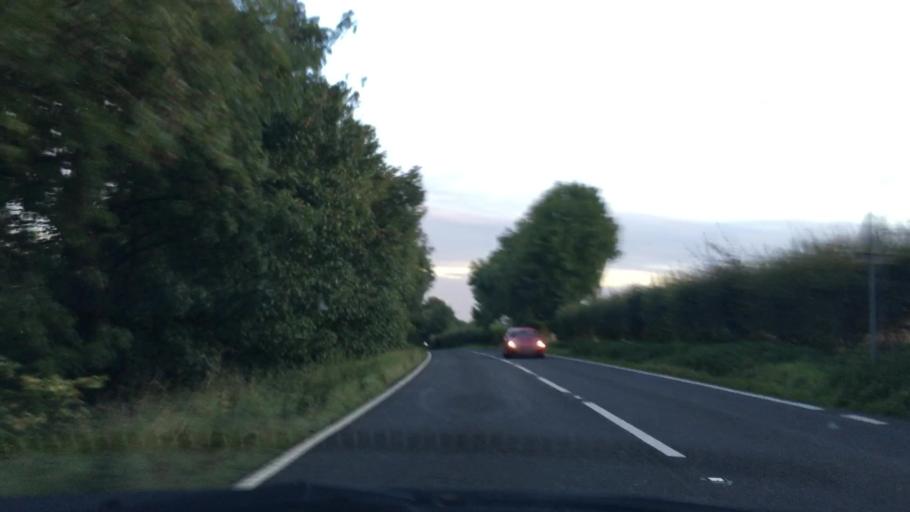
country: GB
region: England
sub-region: North East Lincolnshire
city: Wold Newton
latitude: 53.4768
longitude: -0.1179
